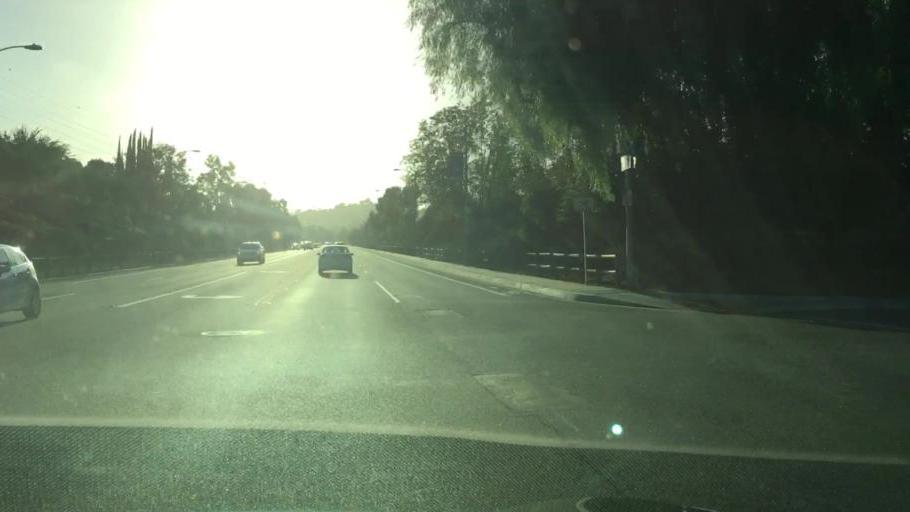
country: US
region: California
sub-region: Los Angeles County
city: Rowland Heights
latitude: 33.9693
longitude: -117.9019
